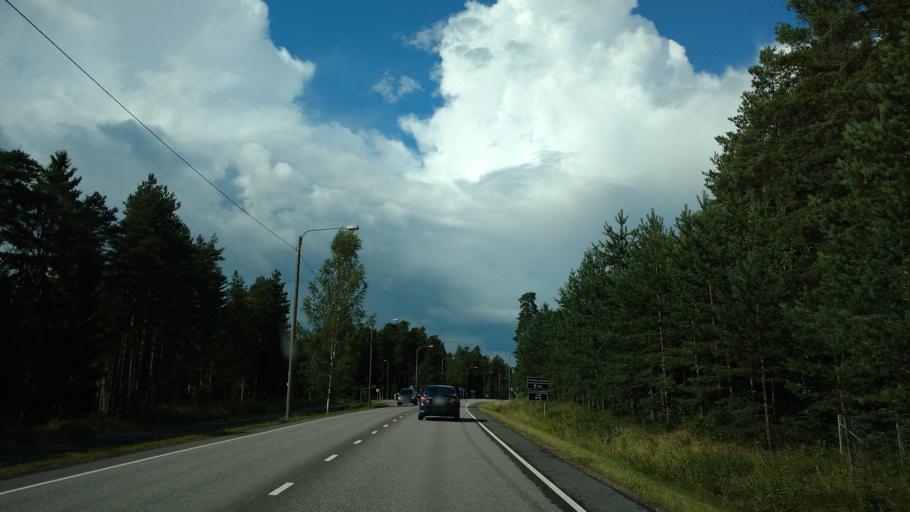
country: FI
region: Varsinais-Suomi
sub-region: Turku
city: Paimio
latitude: 60.4394
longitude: 22.7104
